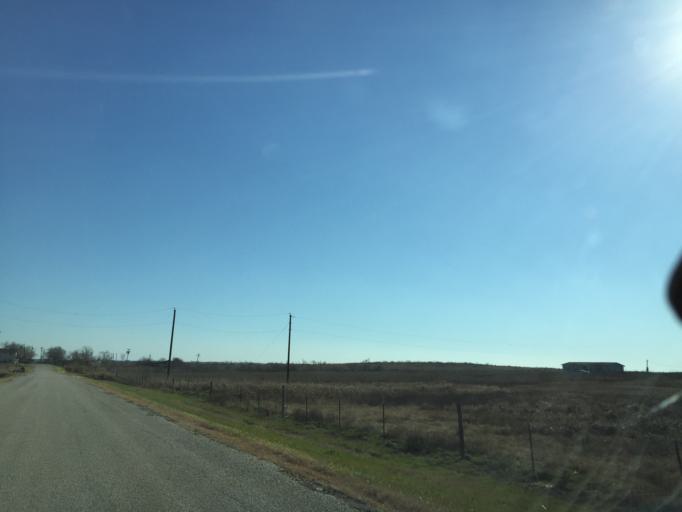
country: US
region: Texas
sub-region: Williamson County
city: Taylor
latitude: 30.5614
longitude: -97.3061
